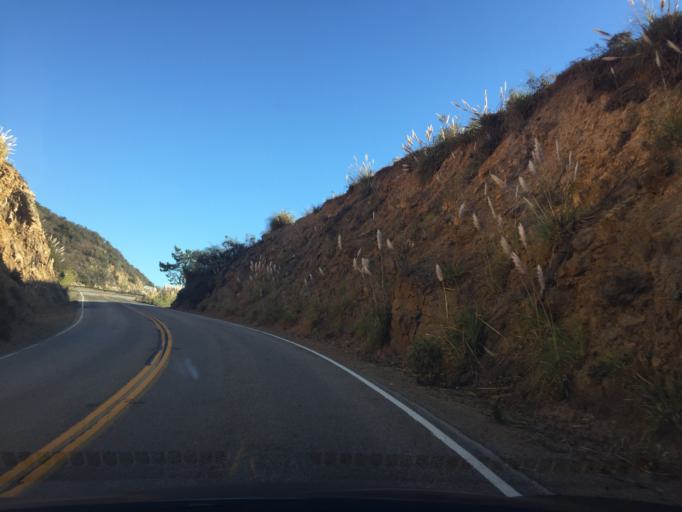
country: US
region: California
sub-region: San Luis Obispo County
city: Cambria
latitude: 35.8324
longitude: -121.3920
